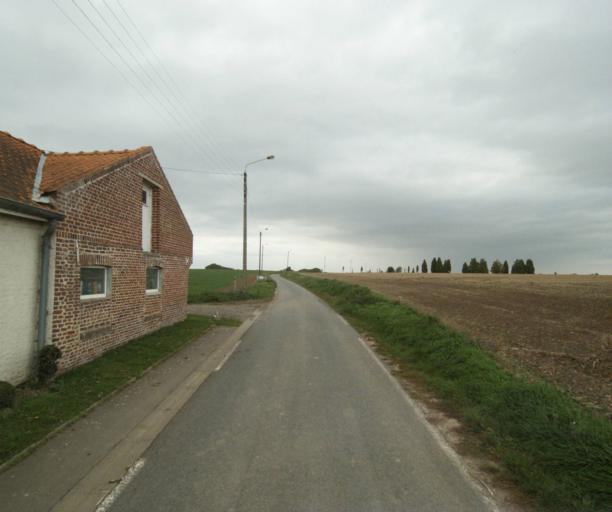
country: FR
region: Nord-Pas-de-Calais
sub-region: Departement du Nord
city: Herlies
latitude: 50.5622
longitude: 2.8510
